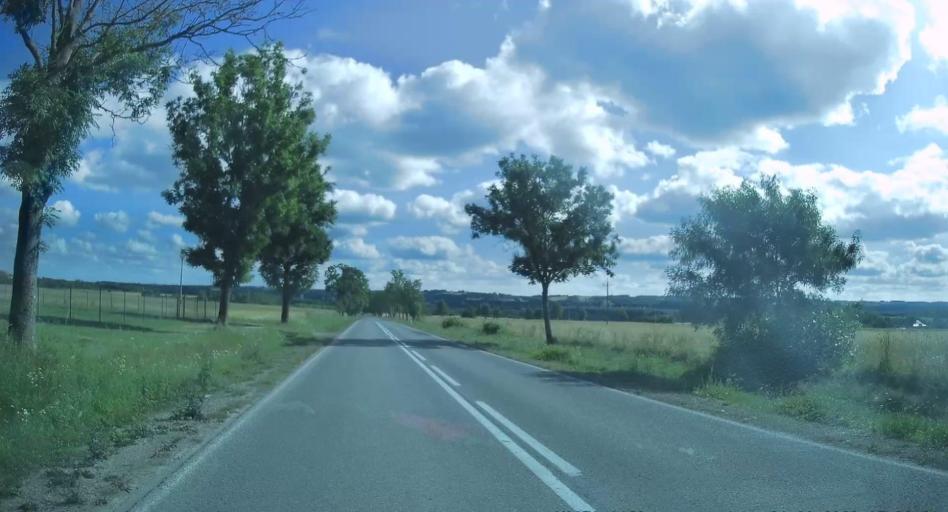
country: PL
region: Swietokrzyskie
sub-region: Powiat kielecki
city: Lagow
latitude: 50.7906
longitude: 21.0817
